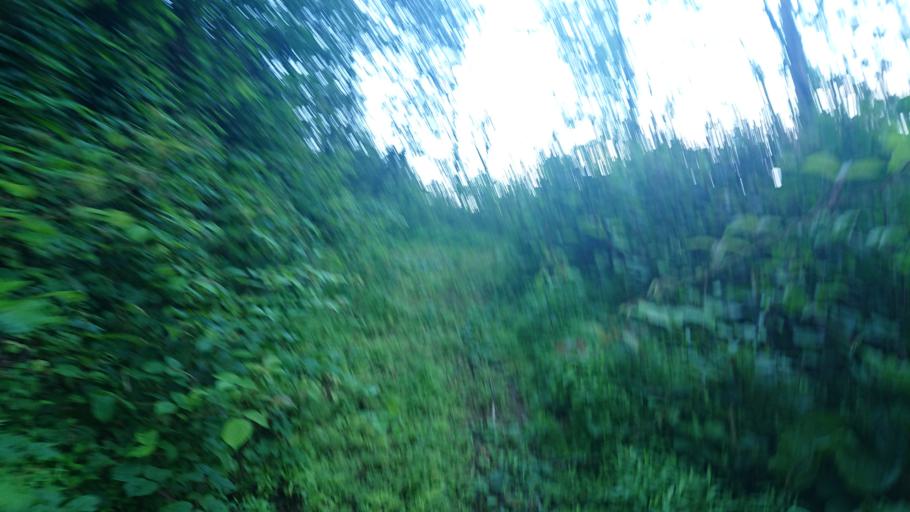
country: TR
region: Rize
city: Rize
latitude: 40.9723
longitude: 40.4953
